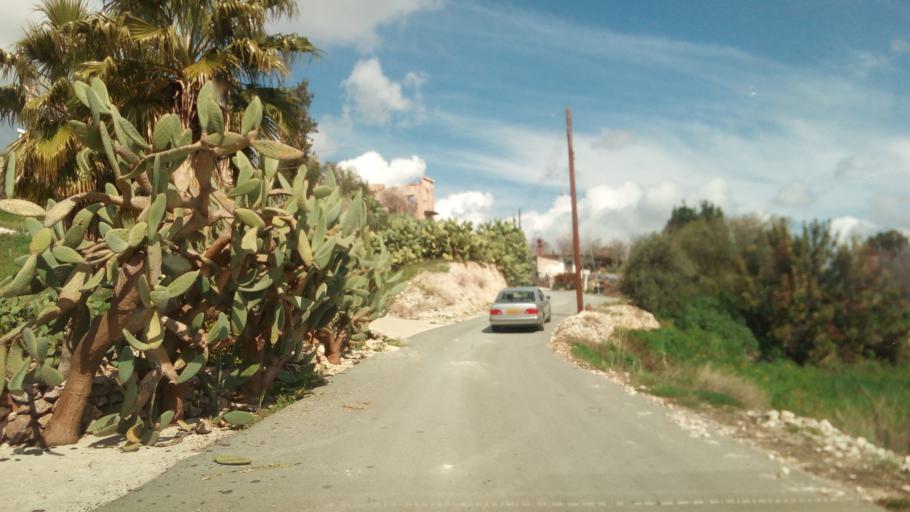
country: CY
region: Pafos
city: Mesogi
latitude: 34.7764
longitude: 32.5713
